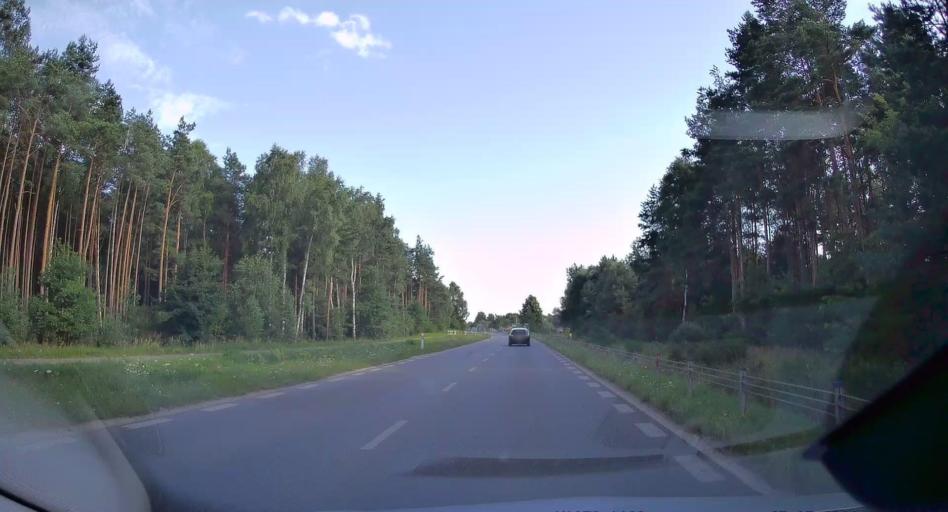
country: PL
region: Swietokrzyskie
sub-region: Powiat konecki
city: Konskie
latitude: 51.1500
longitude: 20.3616
